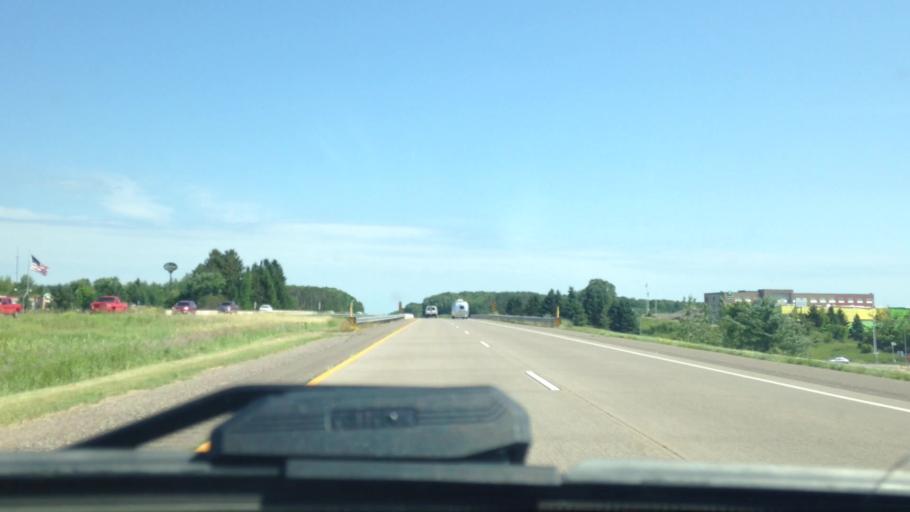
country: US
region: Wisconsin
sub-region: Barron County
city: Rice Lake
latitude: 45.5077
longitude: -91.7621
